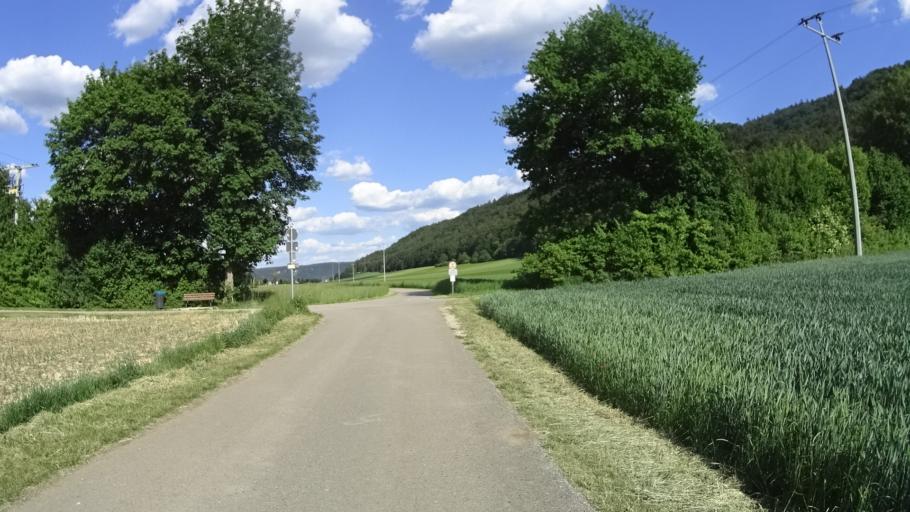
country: DE
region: Bavaria
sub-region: Upper Palatinate
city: Dietfurt
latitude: 49.0185
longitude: 11.4980
